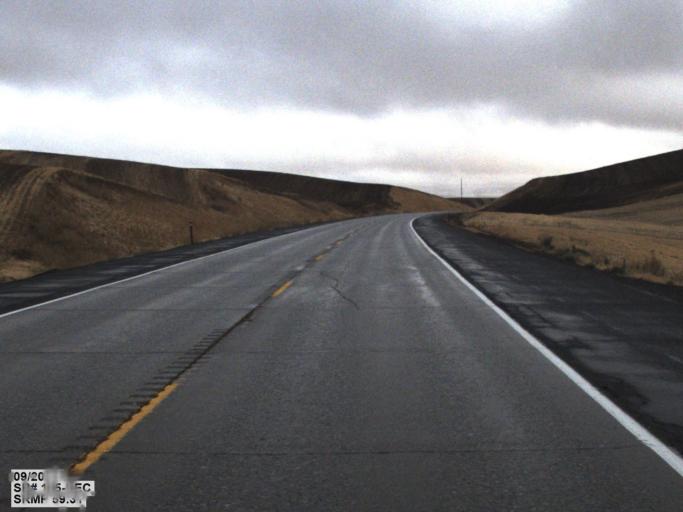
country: US
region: Washington
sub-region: Whitman County
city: Colfax
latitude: 47.1649
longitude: -117.3788
